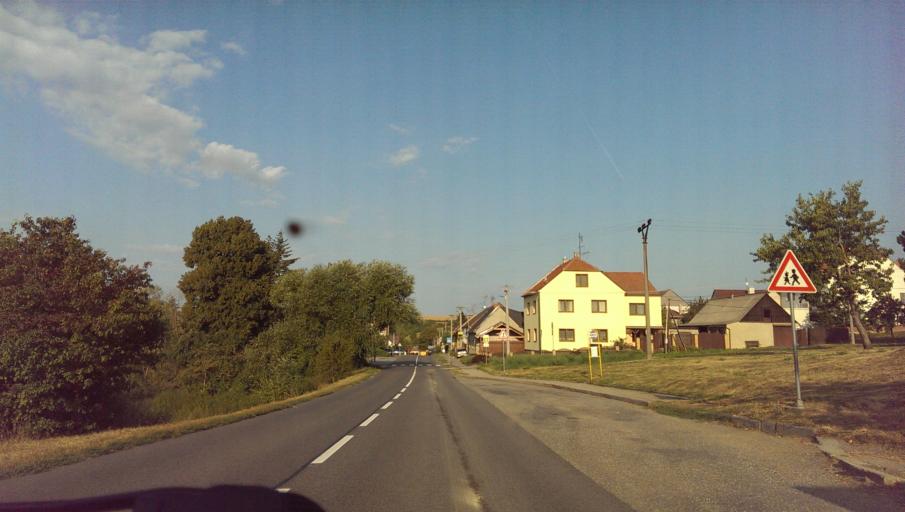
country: CZ
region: South Moravian
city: Zeravice
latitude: 49.0549
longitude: 17.2572
